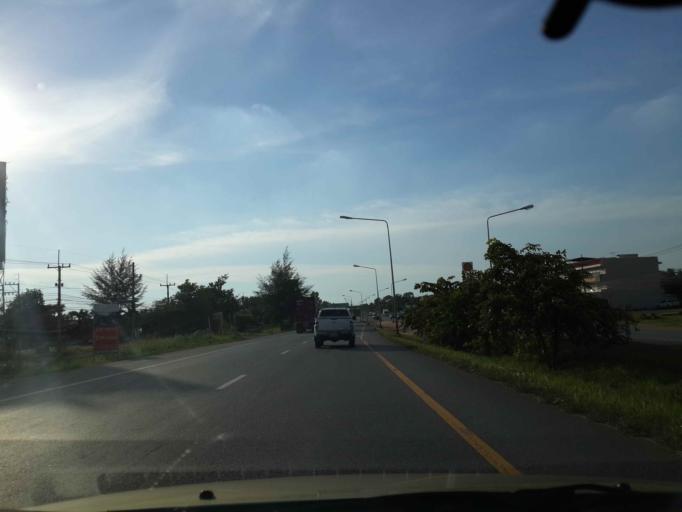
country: TH
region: Chon Buri
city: Bang Lamung
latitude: 12.9939
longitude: 100.9374
